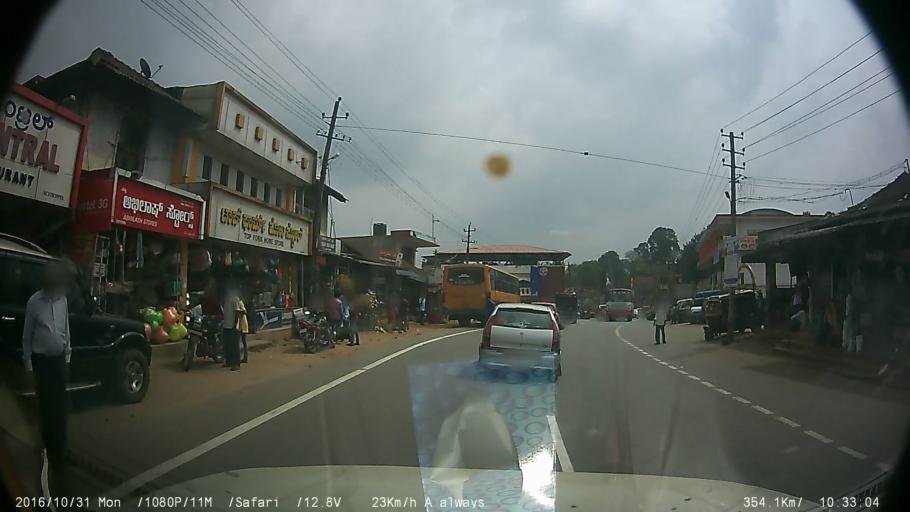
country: IN
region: Karnataka
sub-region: Kodagu
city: Suntikoppa
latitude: 12.4528
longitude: 75.8308
